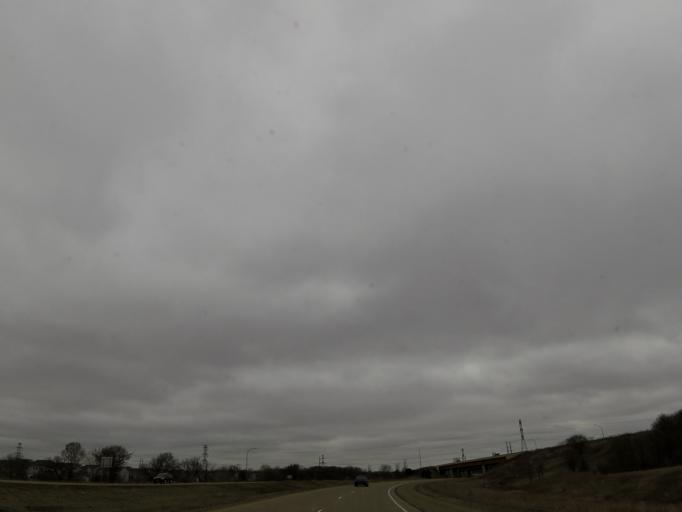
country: US
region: Minnesota
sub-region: Scott County
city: Prior Lake
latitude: 44.7835
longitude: -93.4168
